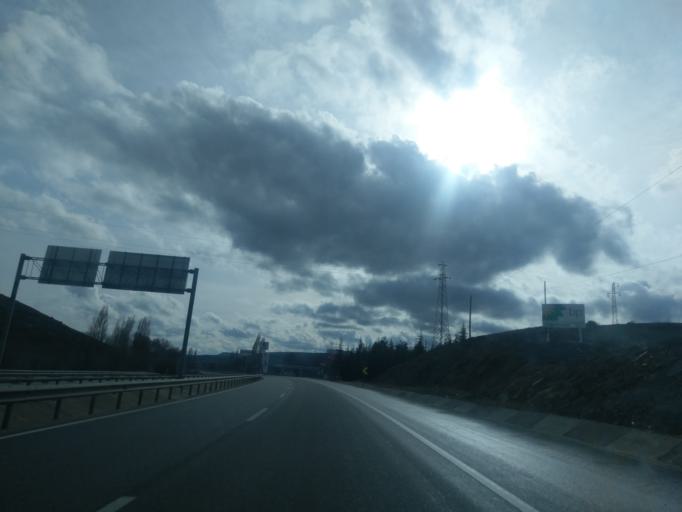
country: TR
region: Eskisehir
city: Inonu
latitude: 39.7048
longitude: 30.1546
